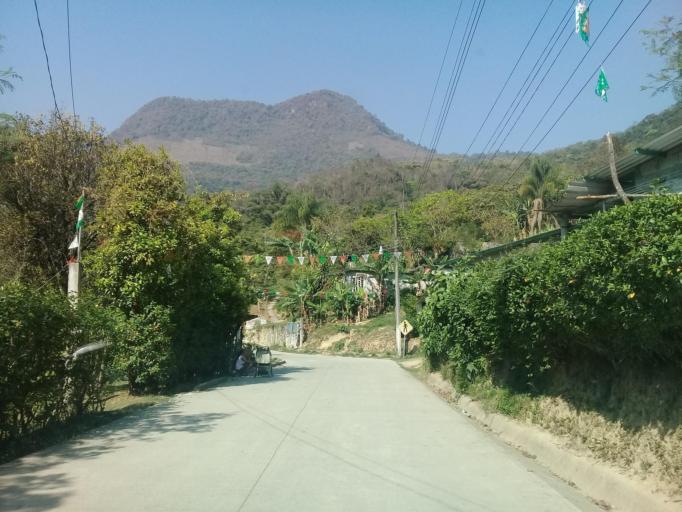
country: MX
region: Veracruz
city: Rafael Delgado
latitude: 18.7825
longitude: -97.0180
